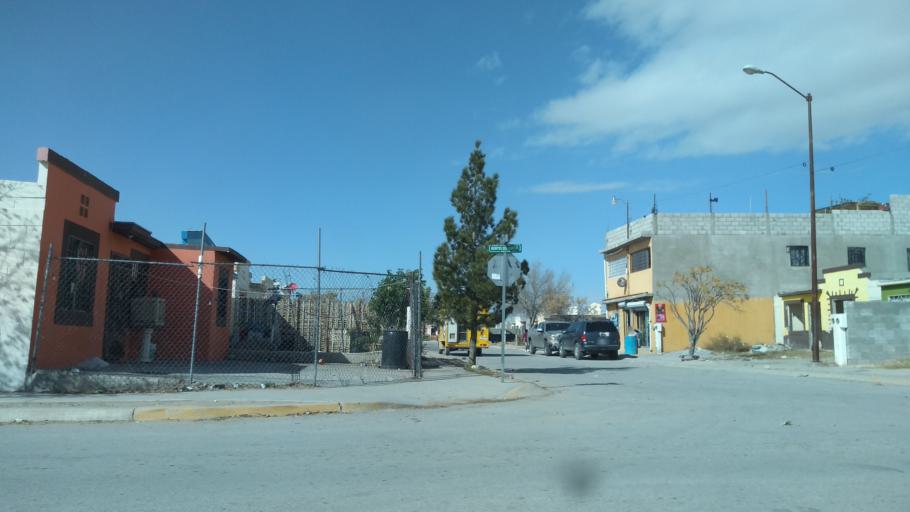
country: US
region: Texas
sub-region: El Paso County
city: San Elizario
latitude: 31.5674
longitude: -106.3323
